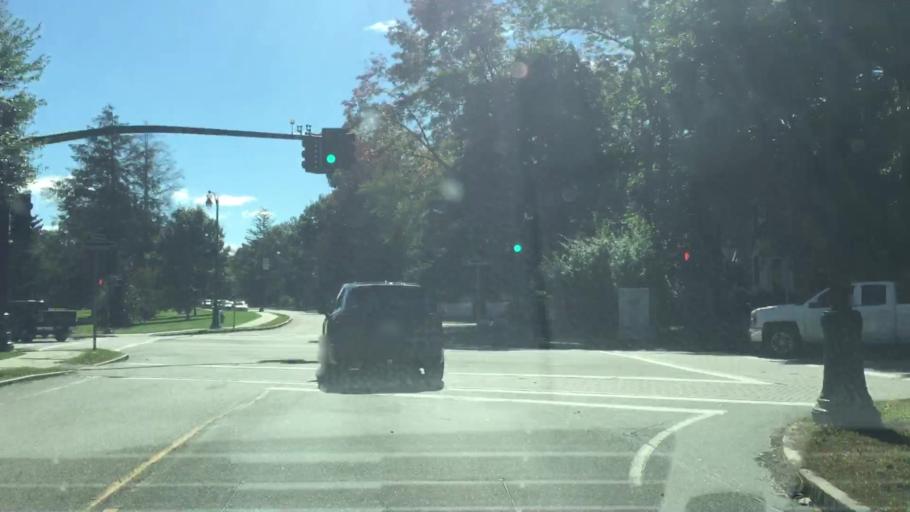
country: US
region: Massachusetts
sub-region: Essex County
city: North Andover
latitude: 42.6860
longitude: -71.1170
